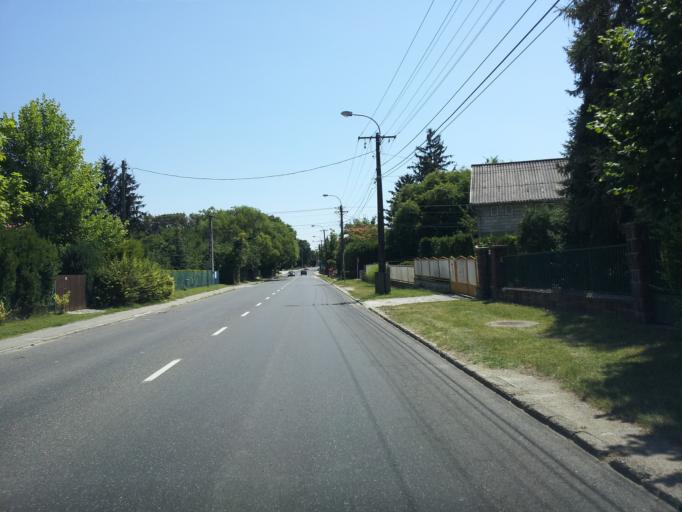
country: HU
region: Veszprem
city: Balatonkenese
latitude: 47.0178
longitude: 18.1621
